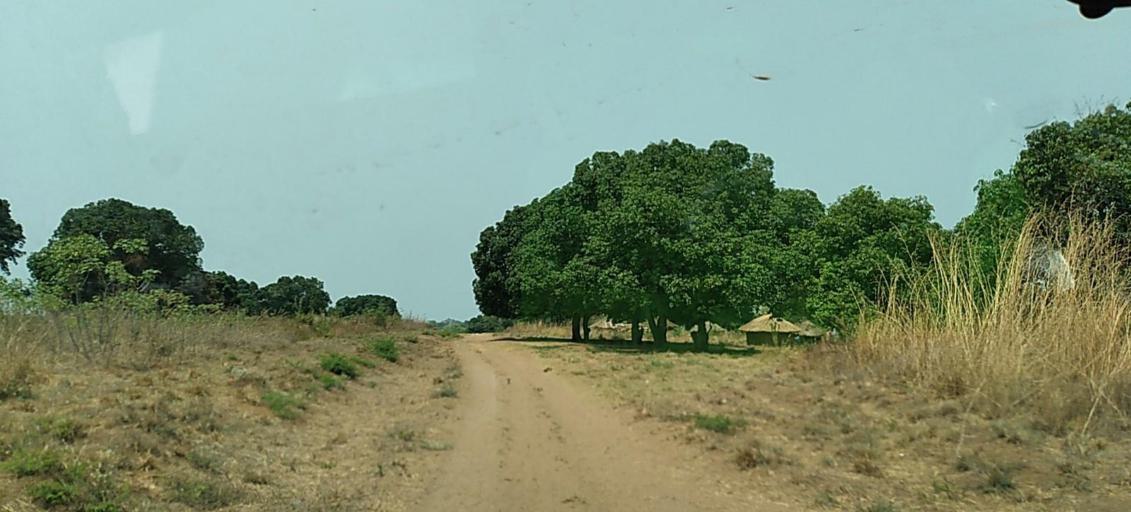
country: ZM
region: Western
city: Lukulu
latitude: -13.9772
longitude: 23.2291
